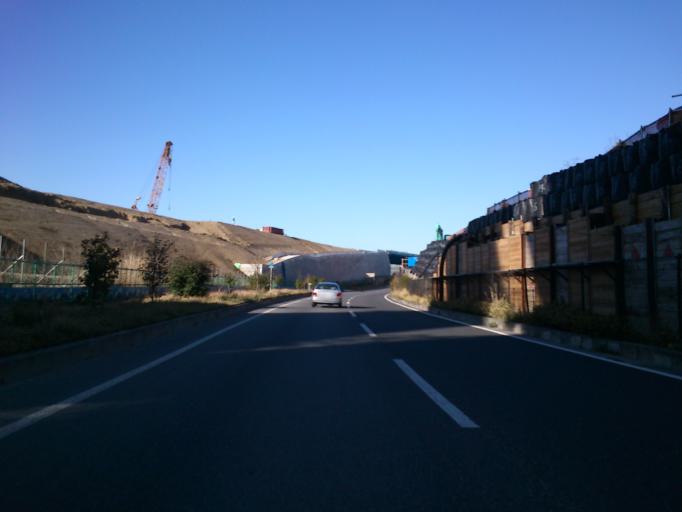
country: JP
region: Kyoto
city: Yawata
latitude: 34.8443
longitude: 135.7238
